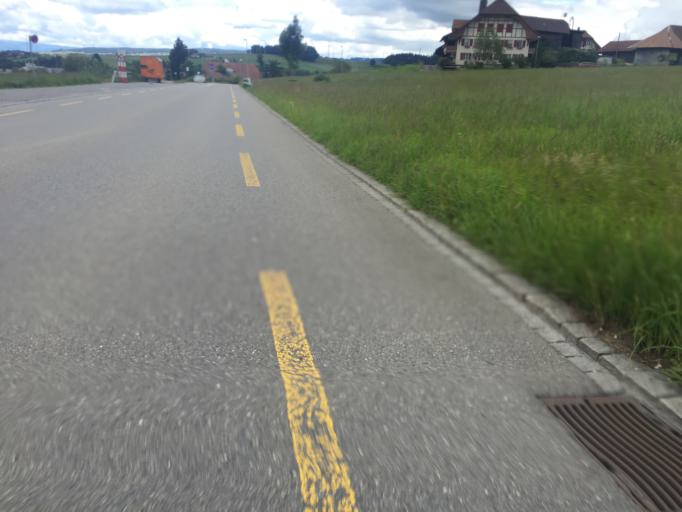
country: CH
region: Bern
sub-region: Bern-Mittelland District
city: Wohlen
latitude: 46.9387
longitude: 7.3707
